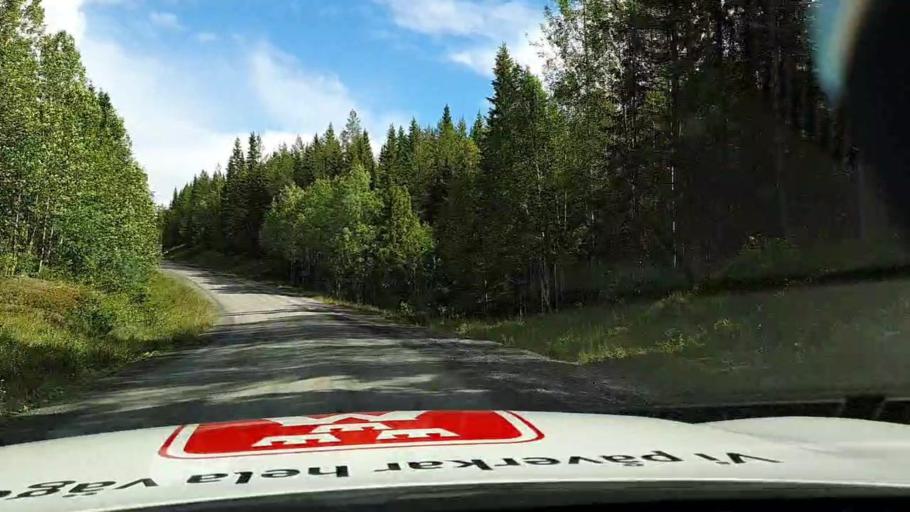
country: SE
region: Jaemtland
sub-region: Krokoms Kommun
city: Valla
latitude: 63.6757
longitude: 13.6903
